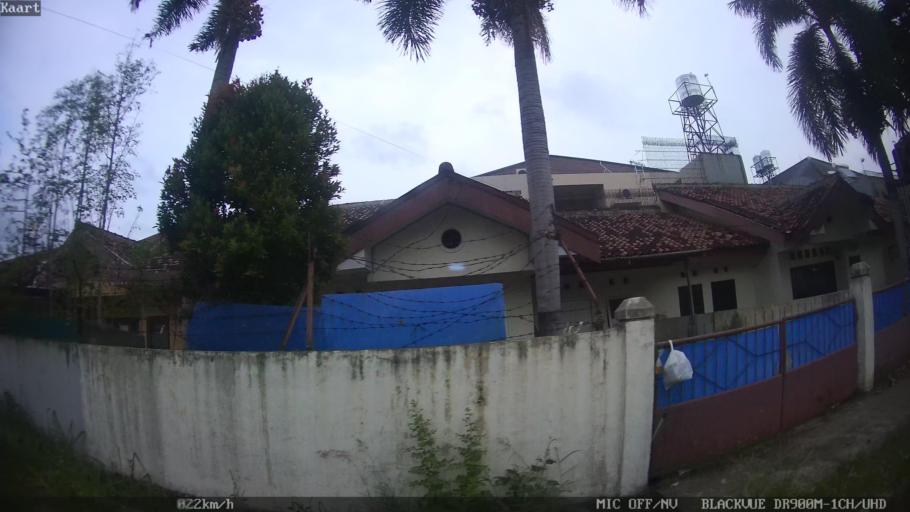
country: ID
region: Lampung
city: Kedaton
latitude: -5.4019
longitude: 105.2695
